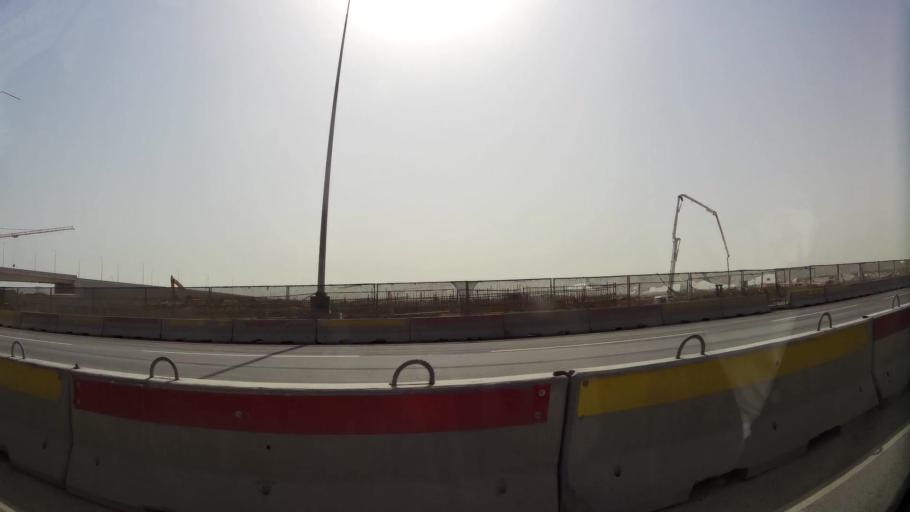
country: QA
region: Baladiyat ad Dawhah
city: Doha
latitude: 25.2243
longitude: 51.5075
